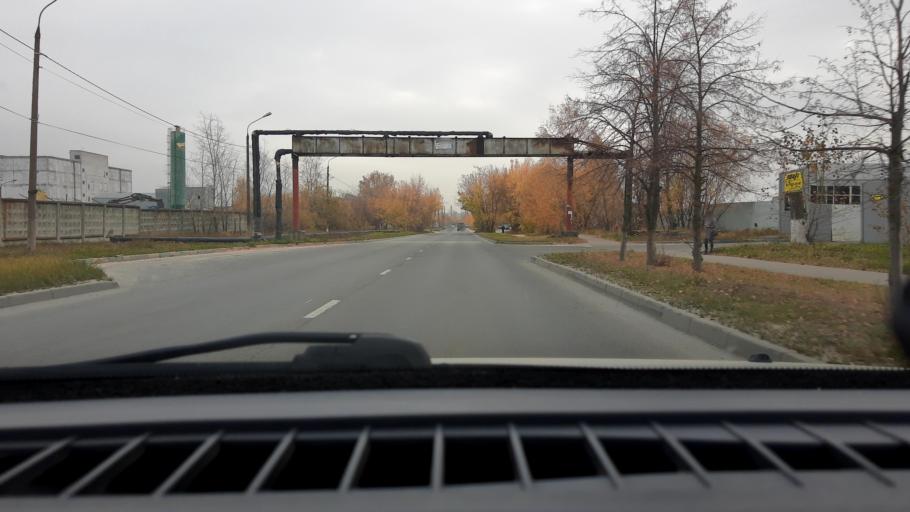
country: RU
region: Nizjnij Novgorod
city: Gorbatovka
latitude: 56.3498
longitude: 43.8094
